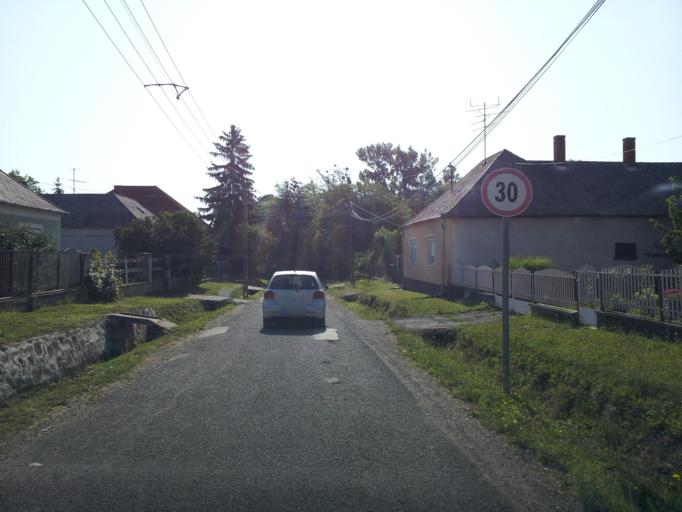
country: HU
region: Zala
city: Cserszegtomaj
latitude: 46.8902
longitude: 17.2257
